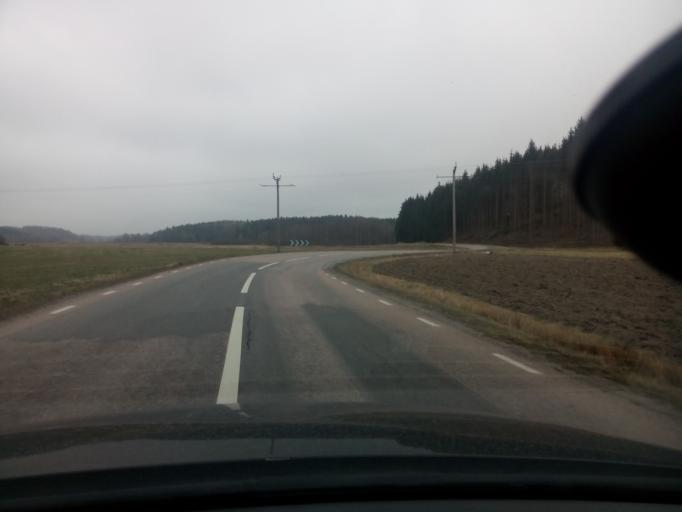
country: SE
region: Soedermanland
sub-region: Gnesta Kommun
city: Gnesta
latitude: 59.0462
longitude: 17.1569
